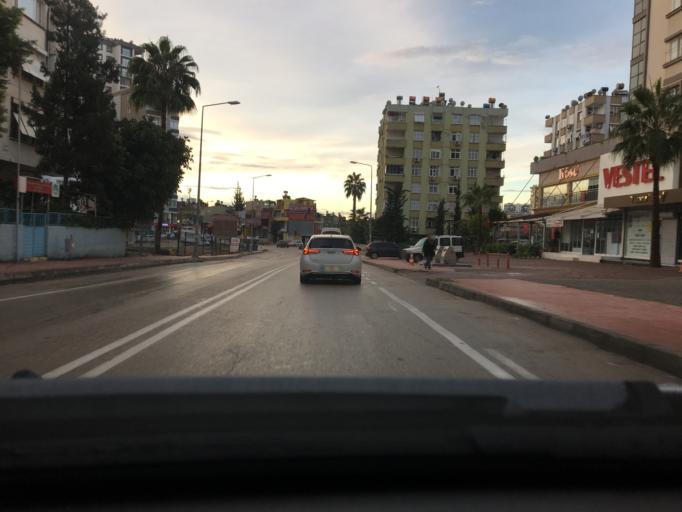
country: TR
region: Adana
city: Seyhan
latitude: 37.0240
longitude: 35.2917
